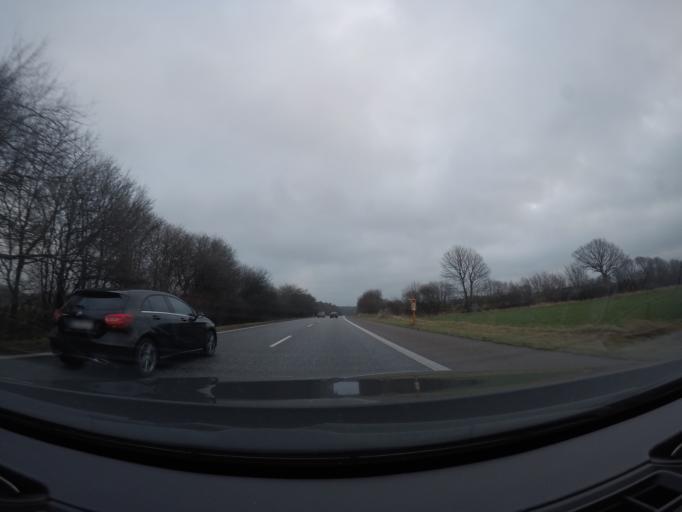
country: DK
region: South Denmark
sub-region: Fredericia Kommune
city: Taulov
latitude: 55.5467
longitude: 9.5545
